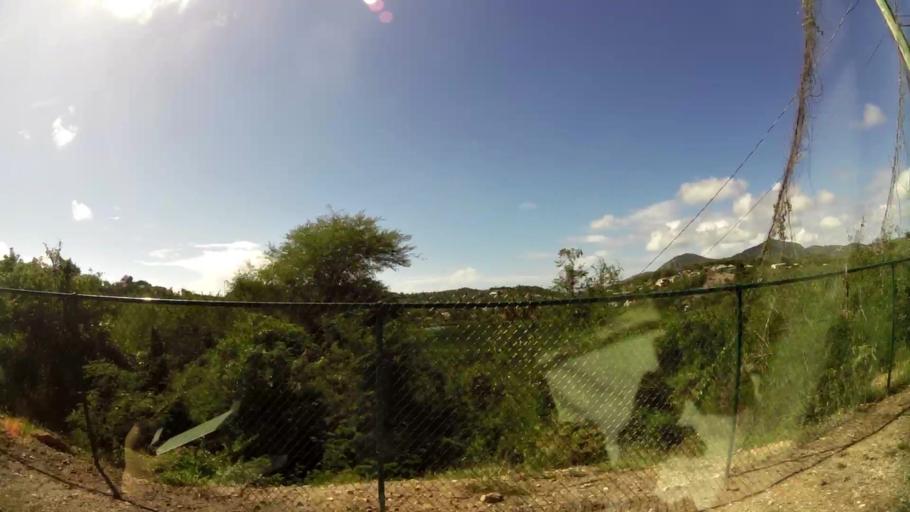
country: AG
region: Saint Paul
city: Falmouth
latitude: 17.0125
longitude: -61.7613
